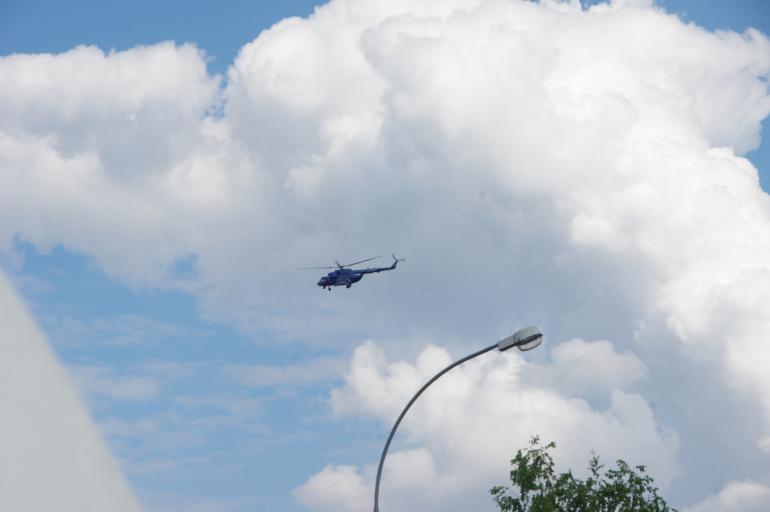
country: RU
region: Moscow
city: Annino
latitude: 55.5705
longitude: 37.5793
